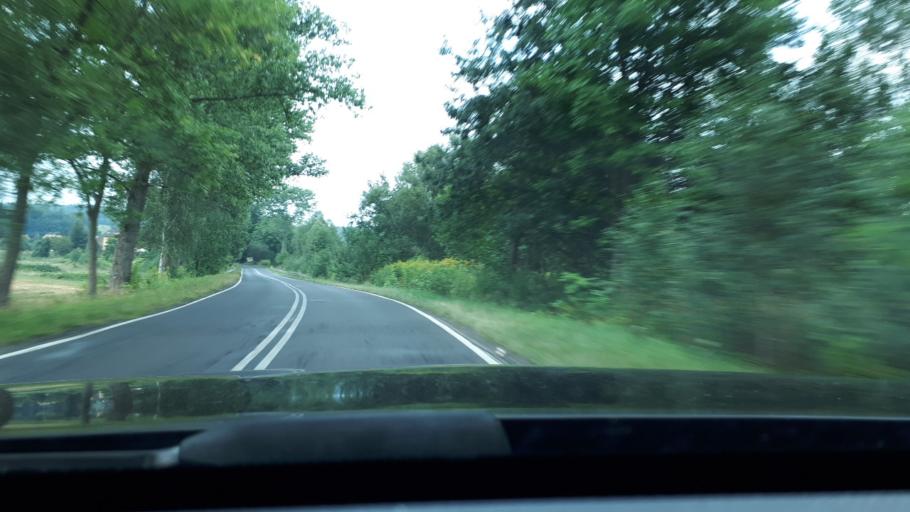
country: PL
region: Lower Silesian Voivodeship
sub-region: Powiat lubanski
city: Lesna
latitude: 51.0439
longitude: 15.2668
